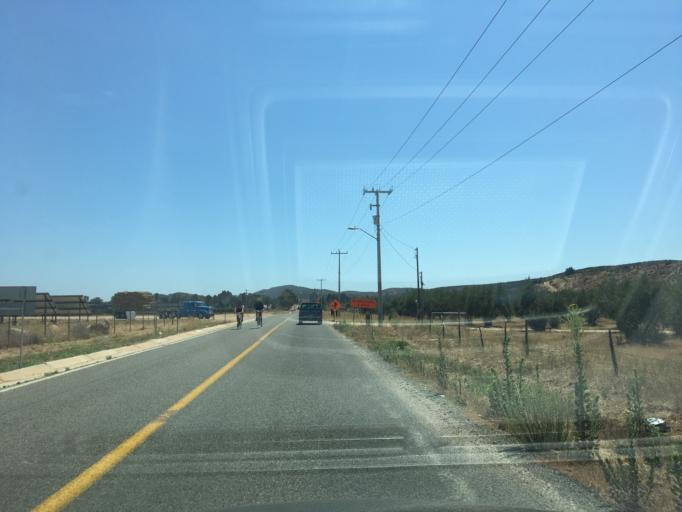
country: MX
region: Baja California
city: El Sauzal
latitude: 32.0060
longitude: -116.6807
